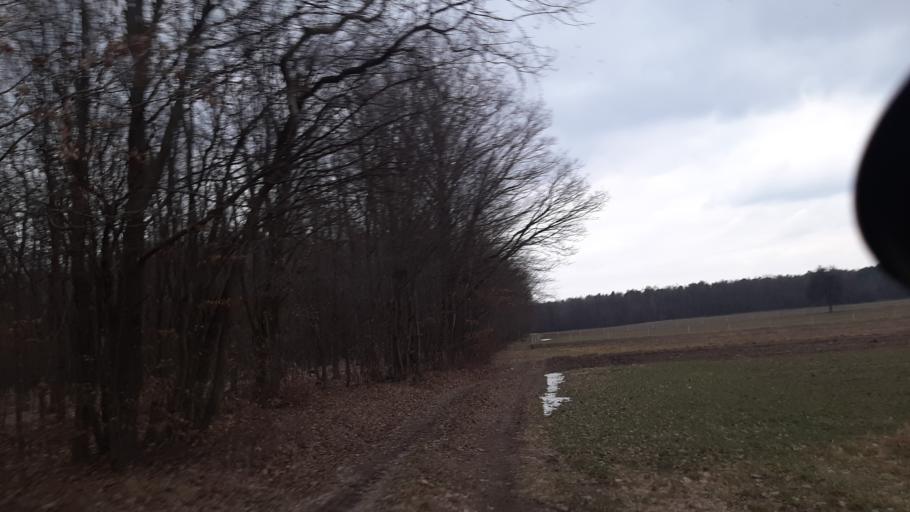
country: PL
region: Lublin Voivodeship
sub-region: Powiat lubelski
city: Garbow
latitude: 51.3902
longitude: 22.4022
